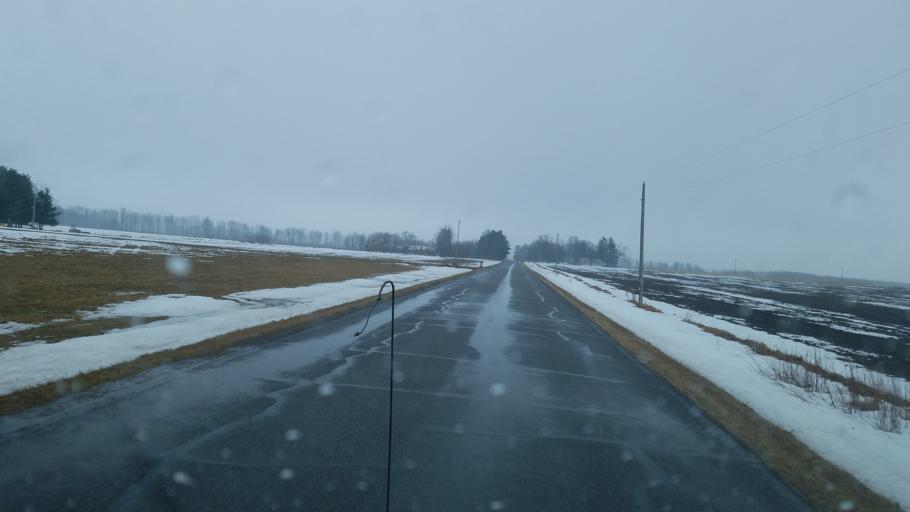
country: US
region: Wisconsin
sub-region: Marathon County
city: Spencer
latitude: 44.6608
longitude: -90.2792
